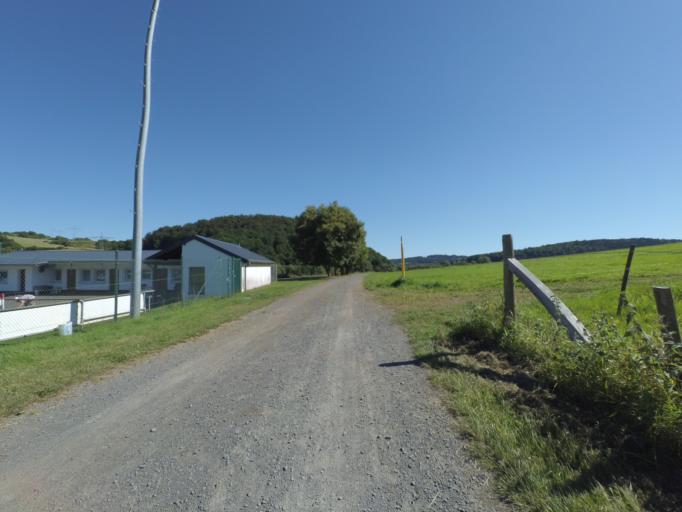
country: DE
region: Rheinland-Pfalz
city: Daun
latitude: 50.2066
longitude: 6.7961
